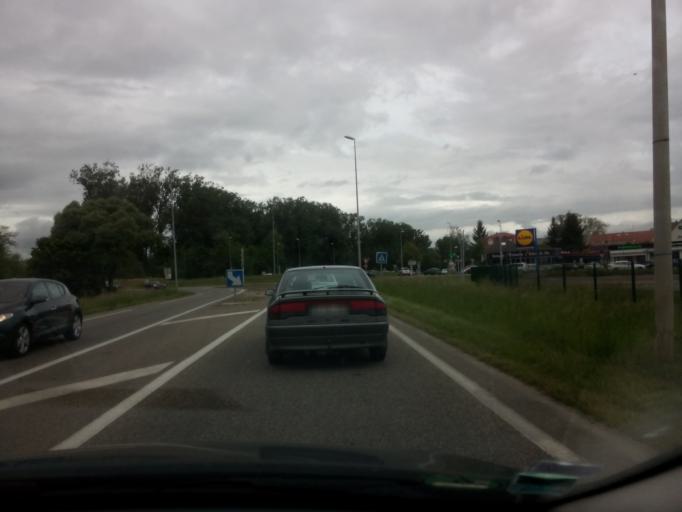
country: FR
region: Alsace
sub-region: Departement du Bas-Rhin
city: Oberhoffen-sur-Moder
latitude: 48.7704
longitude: 7.8699
